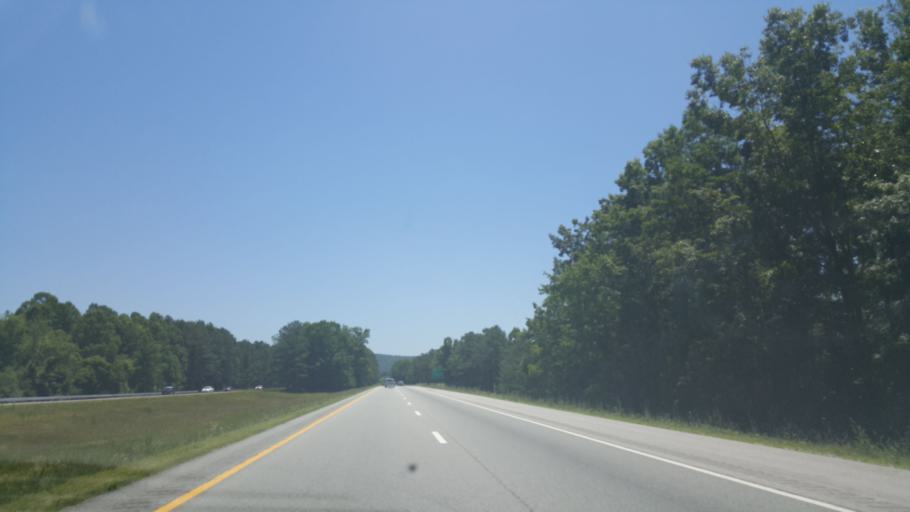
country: US
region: Tennessee
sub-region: Roane County
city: Rockwood
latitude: 35.8947
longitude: -84.7558
